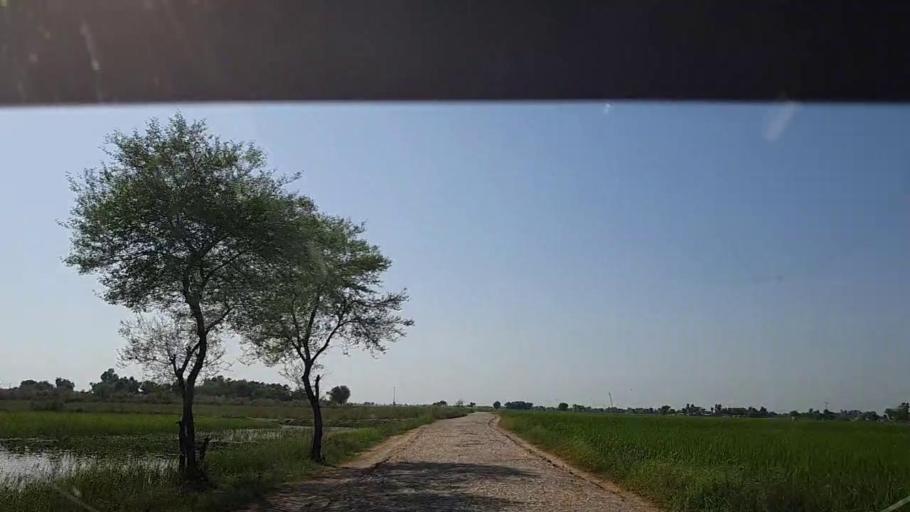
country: PK
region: Sindh
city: Ghauspur
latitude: 28.1806
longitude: 69.0308
